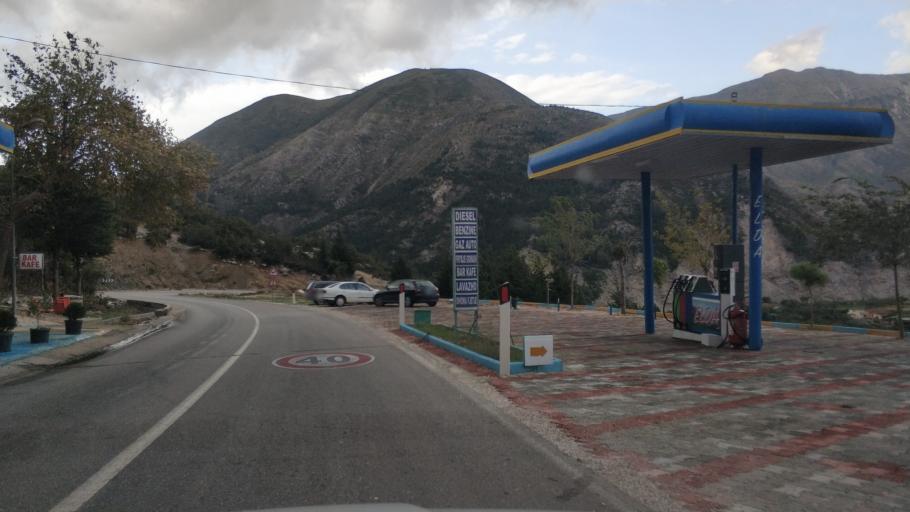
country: AL
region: Vlore
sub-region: Rrethi i Vlores
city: Orikum
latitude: 40.2414
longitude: 19.5506
